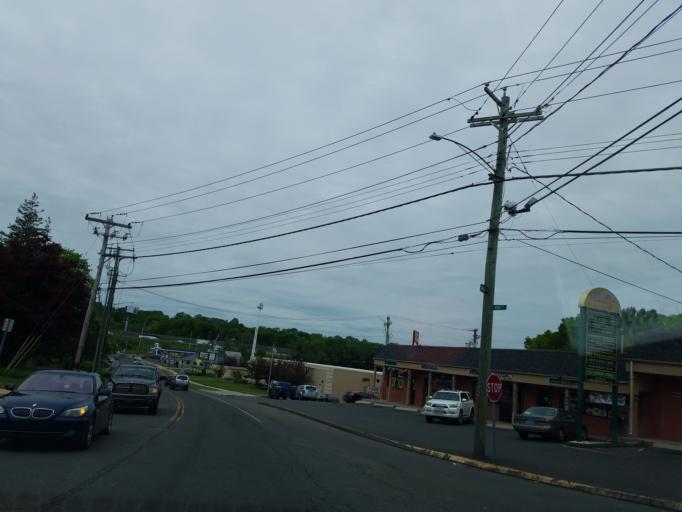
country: US
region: Connecticut
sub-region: New Haven County
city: West Haven
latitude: 41.2740
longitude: -72.9647
